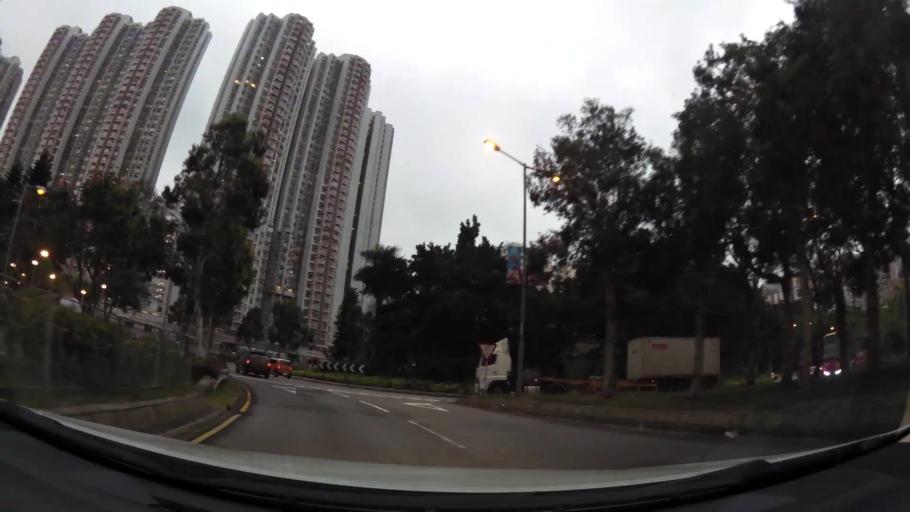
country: HK
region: Tsuen Wan
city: Tsuen Wan
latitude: 22.3535
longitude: 114.1071
